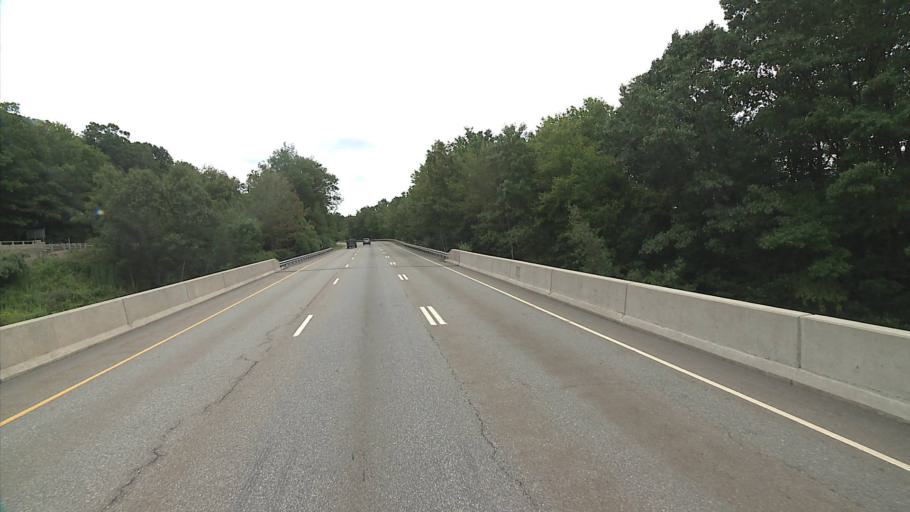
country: US
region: Connecticut
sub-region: Litchfield County
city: Thomaston
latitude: 41.6922
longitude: -73.0690
